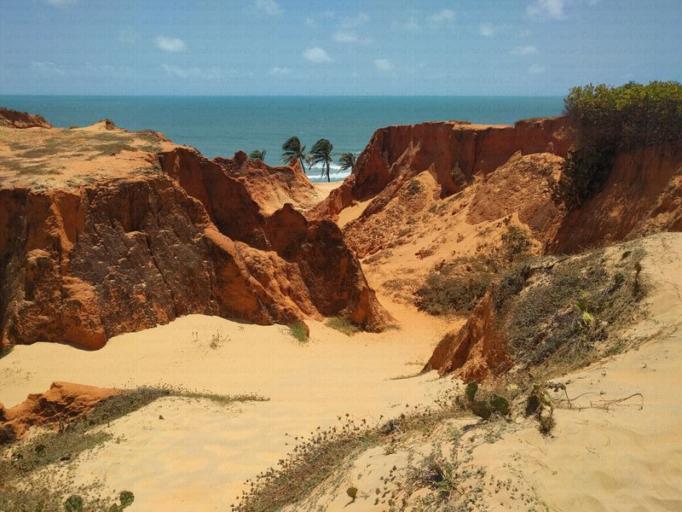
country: BR
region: Ceara
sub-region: Beberibe
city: Beberibe
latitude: -4.1558
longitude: -38.1088
